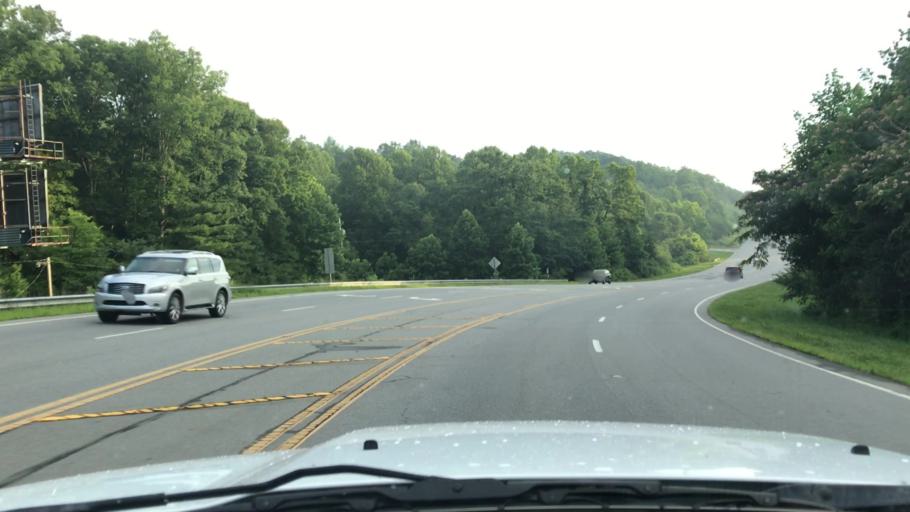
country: US
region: North Carolina
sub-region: Cherokee County
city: Murphy
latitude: 35.0264
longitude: -84.1116
